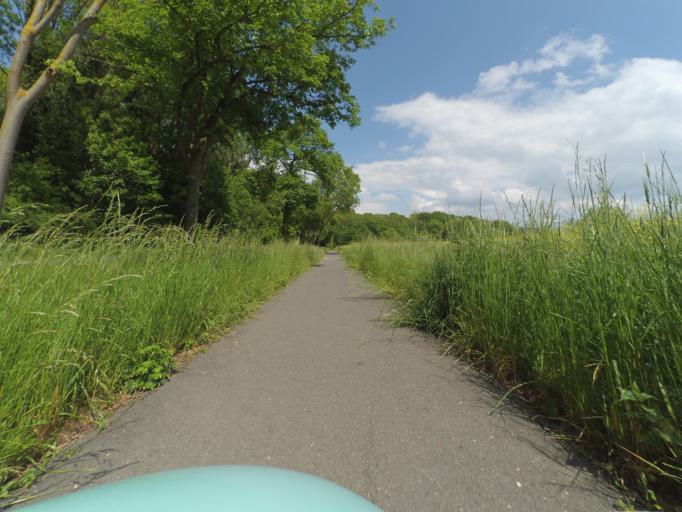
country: DE
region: Lower Saxony
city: Lehrte
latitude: 52.3584
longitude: 9.9499
